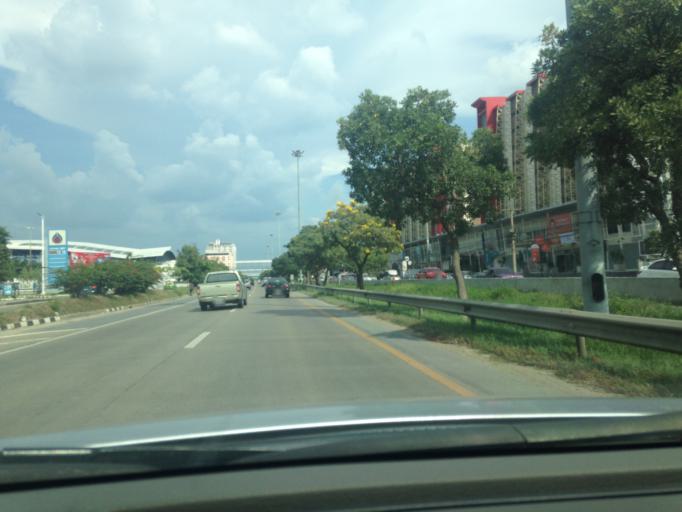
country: TH
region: Pathum Thani
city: Khlong Luang
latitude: 14.0656
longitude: 100.5979
